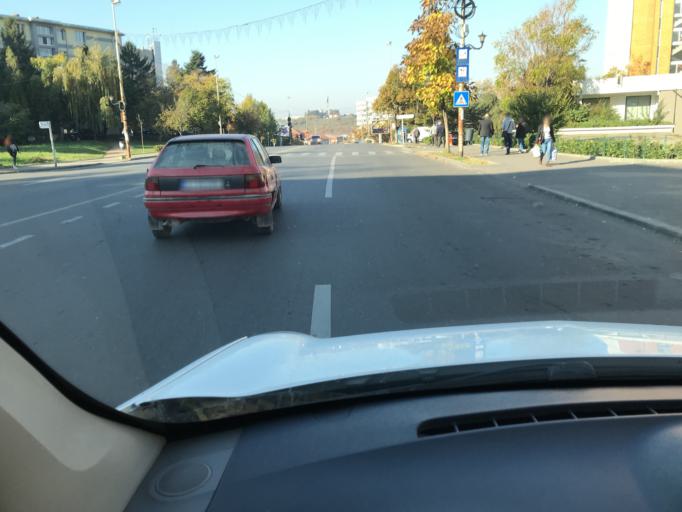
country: RO
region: Olt
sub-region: Municipiul Slatina
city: Slatina
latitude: 44.4317
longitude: 24.3659
